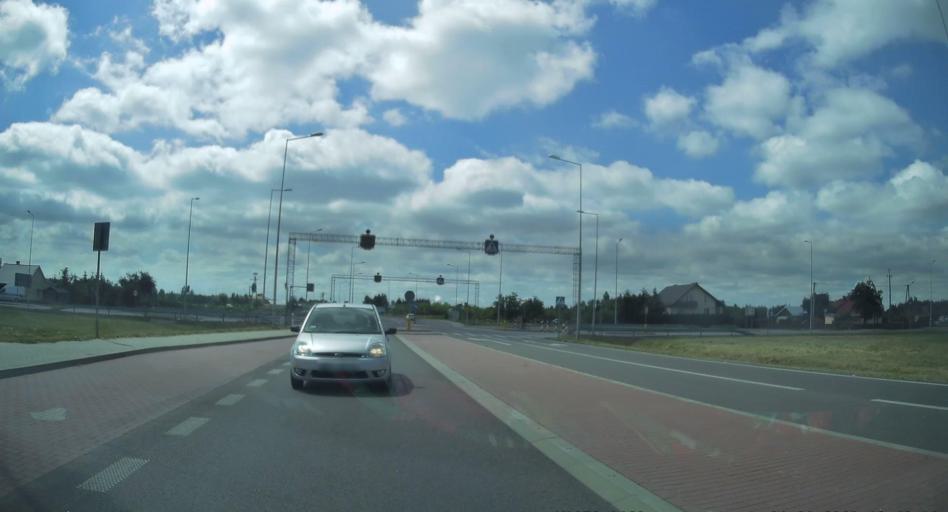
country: PL
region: Subcarpathian Voivodeship
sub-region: Powiat mielecki
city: Mielec
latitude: 50.3300
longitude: 21.4871
